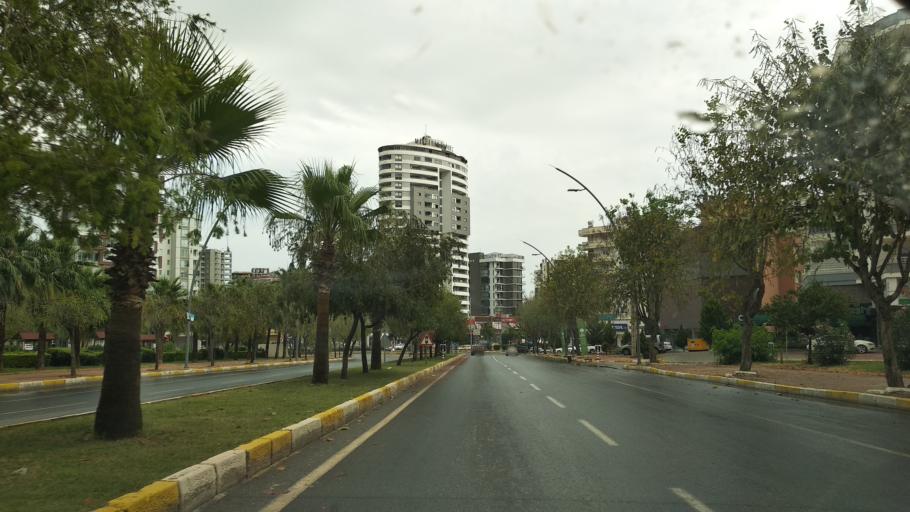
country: TR
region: Mersin
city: Mercin
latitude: 36.7990
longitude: 34.5936
